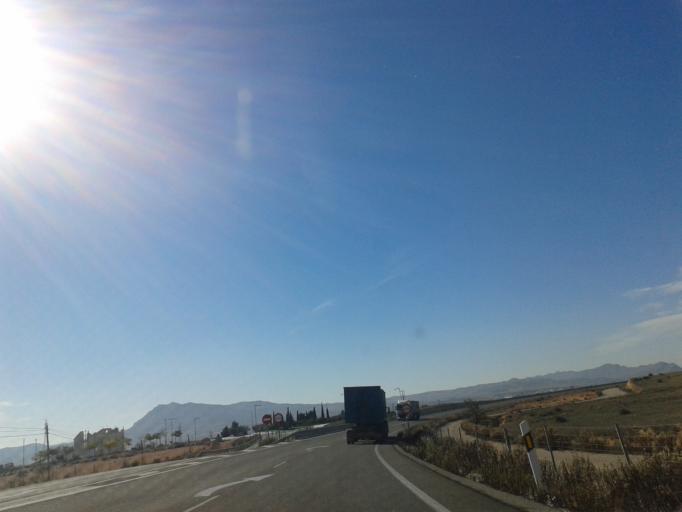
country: ES
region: Castille-La Mancha
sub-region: Provincia de Albacete
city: Caudete
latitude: 38.7192
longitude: -0.9544
